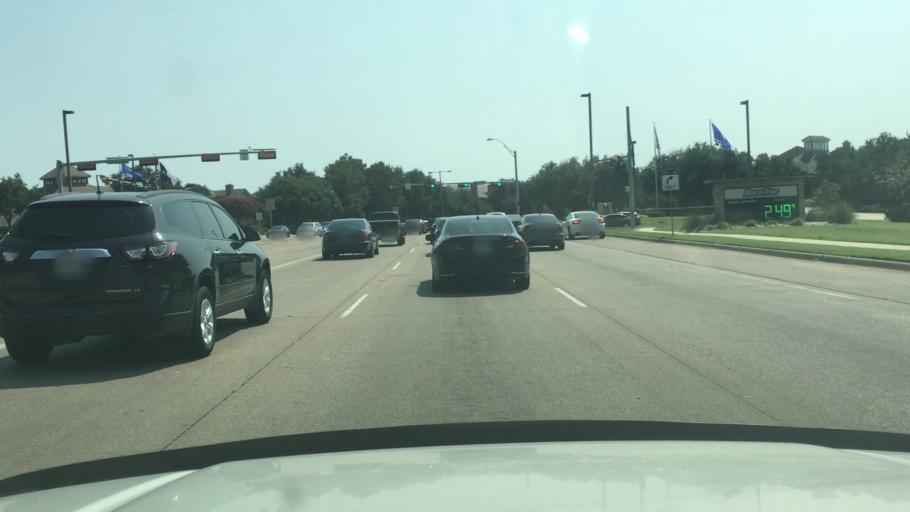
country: US
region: Texas
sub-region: Dallas County
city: Farmers Branch
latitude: 32.8966
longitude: -96.9589
